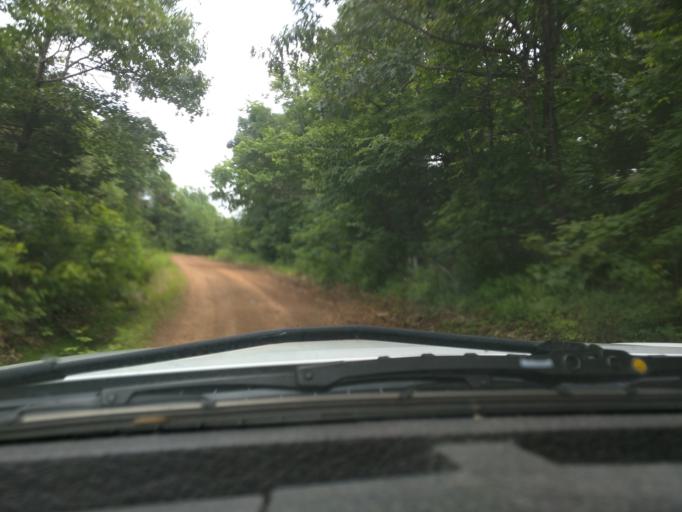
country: US
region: Arkansas
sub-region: Madison County
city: Huntsville
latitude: 35.8898
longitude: -93.5682
